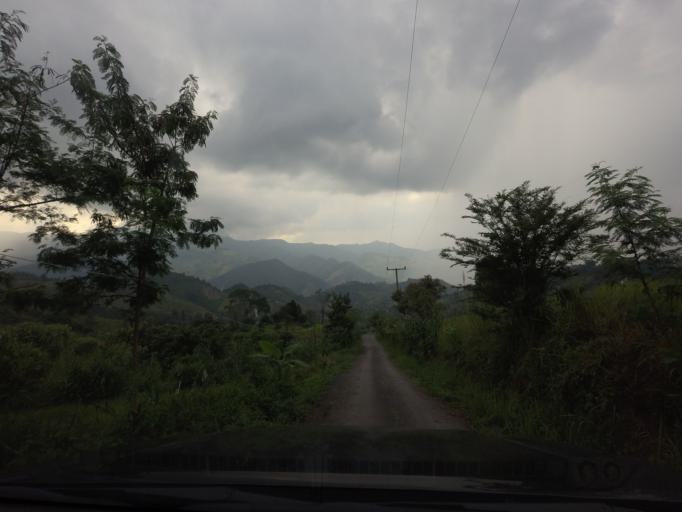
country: TH
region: Nan
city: Bo Kluea
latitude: 19.3502
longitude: 101.1790
